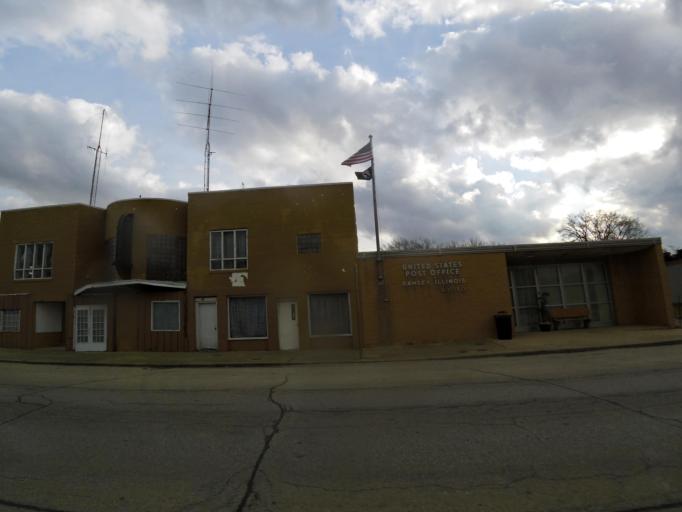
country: US
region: Illinois
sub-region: Fayette County
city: Ramsey
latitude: 39.1418
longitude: -89.1083
